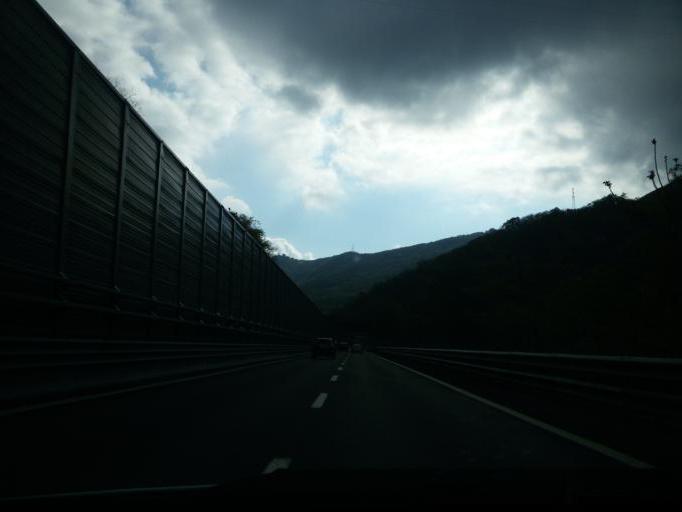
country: IT
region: Liguria
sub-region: Provincia di Genova
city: Genoa
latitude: 44.4457
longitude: 8.9099
